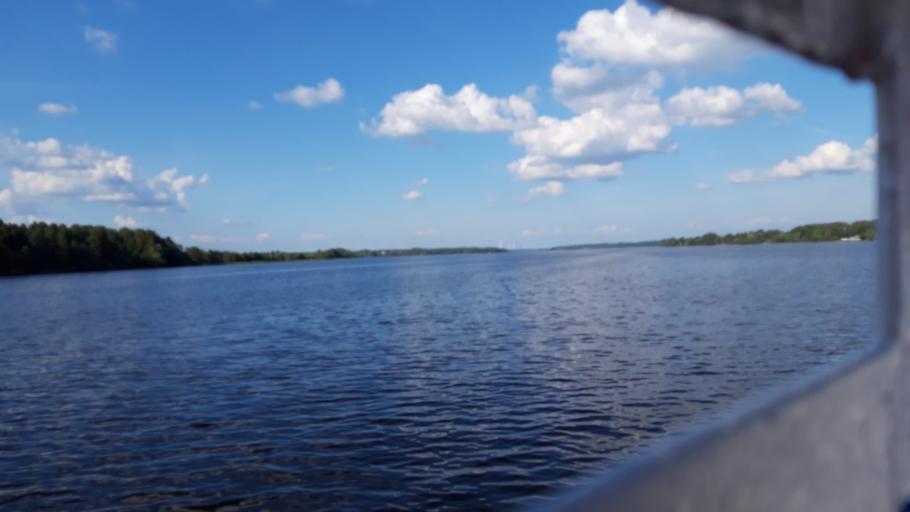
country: RU
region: Tverskaya
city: Konakovo
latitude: 56.6535
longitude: 36.6326
